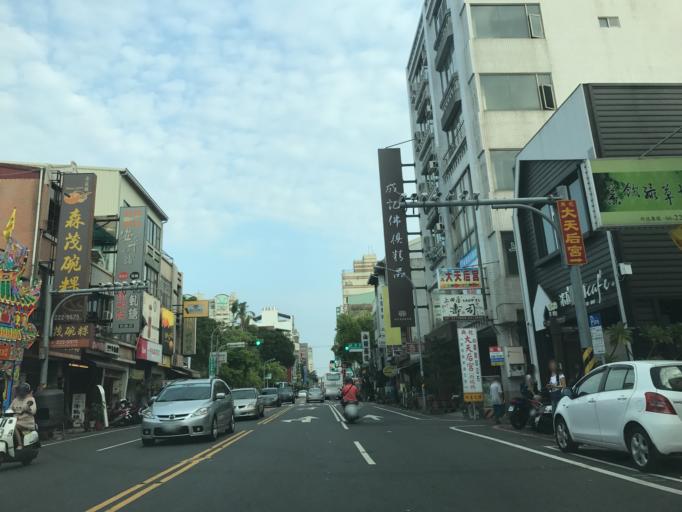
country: TW
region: Taiwan
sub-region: Tainan
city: Tainan
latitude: 22.9971
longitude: 120.2015
